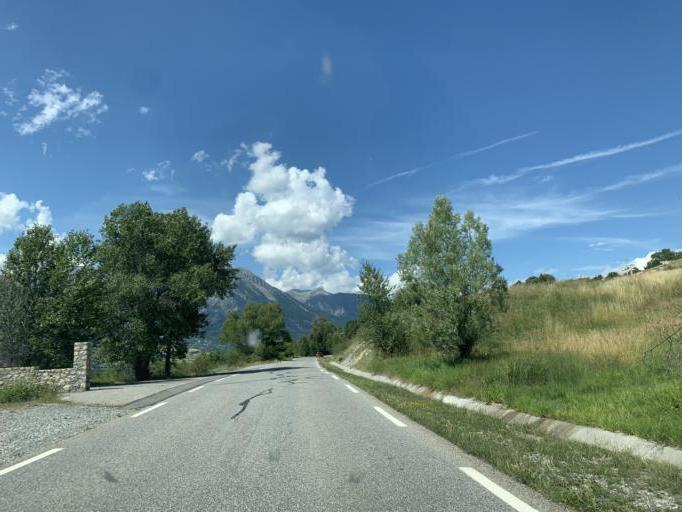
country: FR
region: Provence-Alpes-Cote d'Azur
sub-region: Departement des Hautes-Alpes
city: Embrun
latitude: 44.5707
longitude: 6.5229
